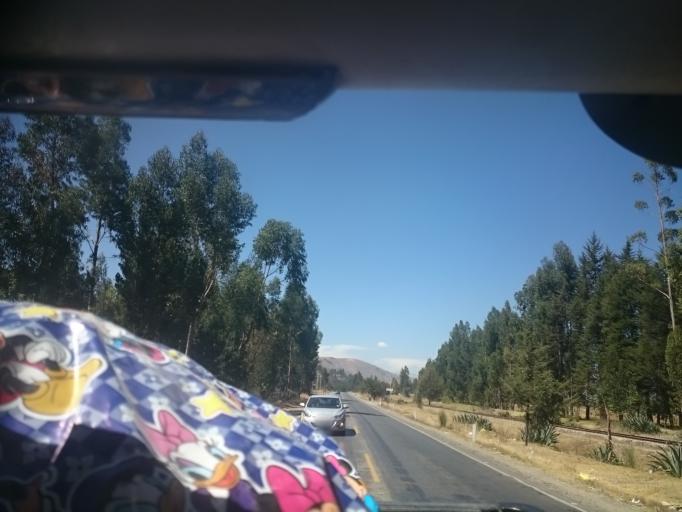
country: PE
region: Junin
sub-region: Provincia de Jauja
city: Ataura
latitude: -11.7949
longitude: -75.4546
